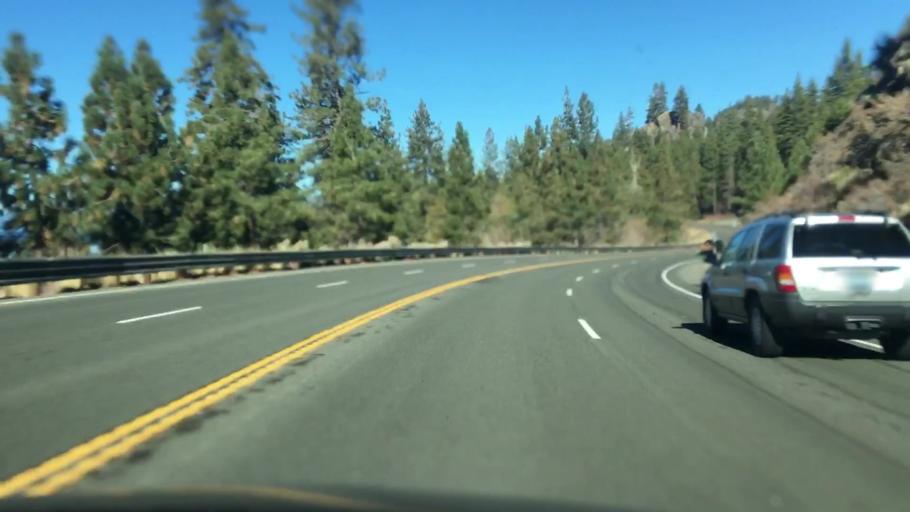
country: US
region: Nevada
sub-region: Douglas County
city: Kingsbury
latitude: 39.0603
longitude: -119.9426
